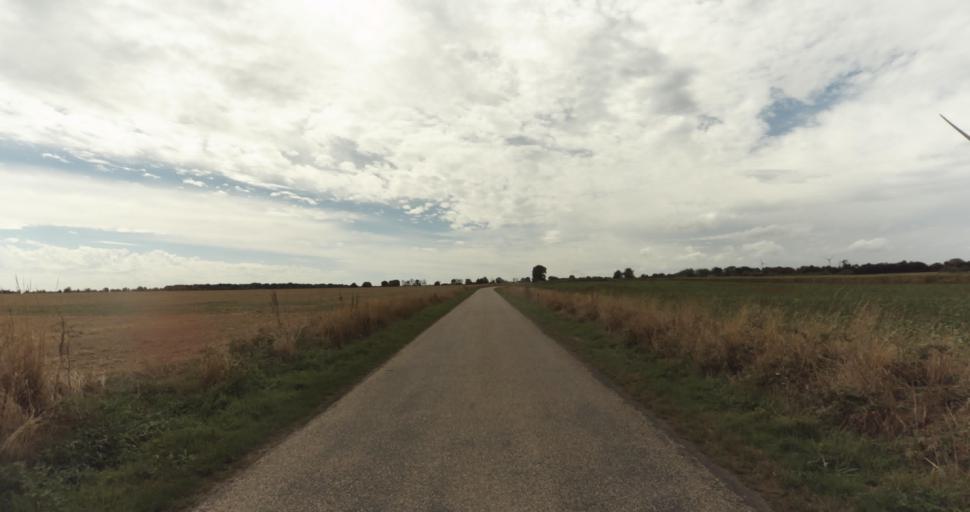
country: FR
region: Lower Normandy
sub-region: Departement du Calvados
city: La Vespiere
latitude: 48.9645
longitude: 0.3726
